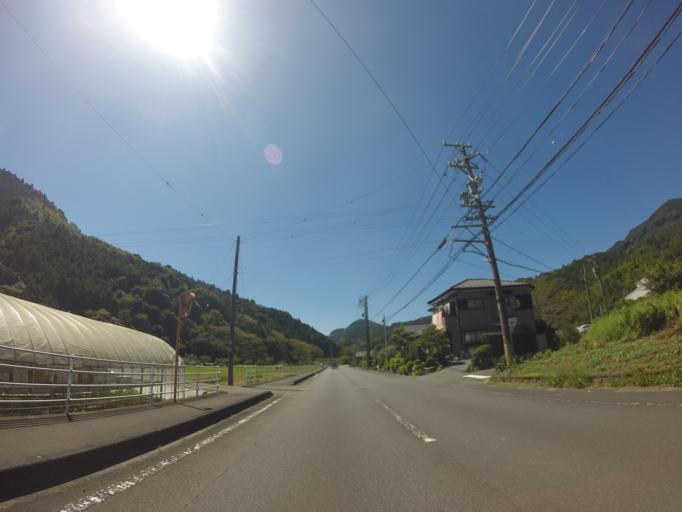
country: JP
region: Shizuoka
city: Fujieda
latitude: 34.9382
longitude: 138.2085
